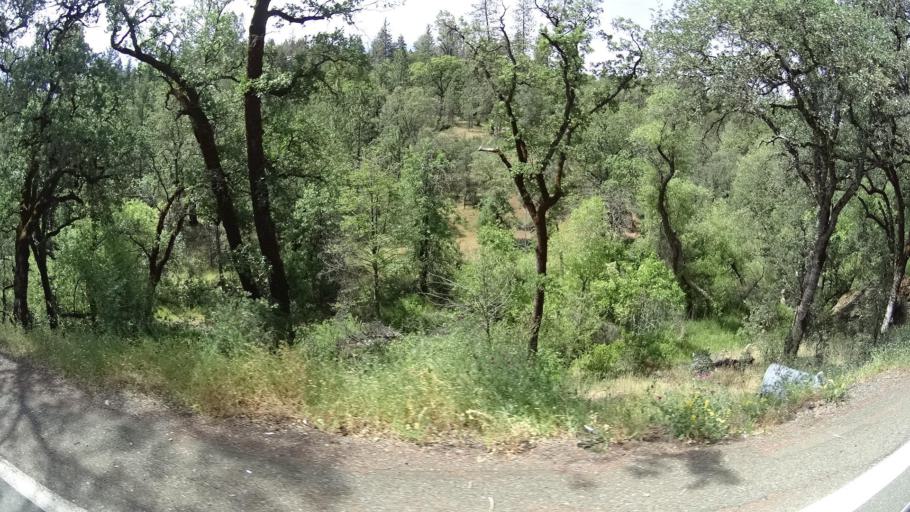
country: US
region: California
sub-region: Lake County
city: Lower Lake
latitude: 38.8834
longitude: -122.6677
